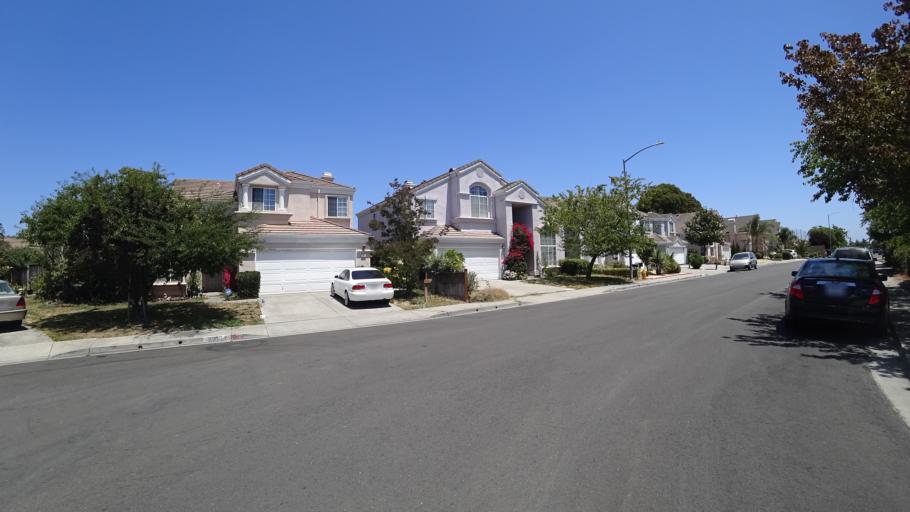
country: US
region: California
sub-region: Alameda County
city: Hayward
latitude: 37.6281
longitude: -122.0571
